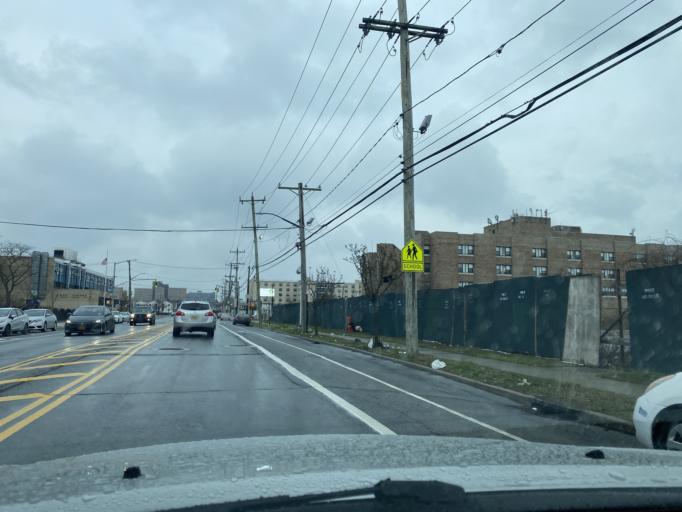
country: US
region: New York
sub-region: Nassau County
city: Inwood
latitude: 40.5952
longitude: -73.7829
